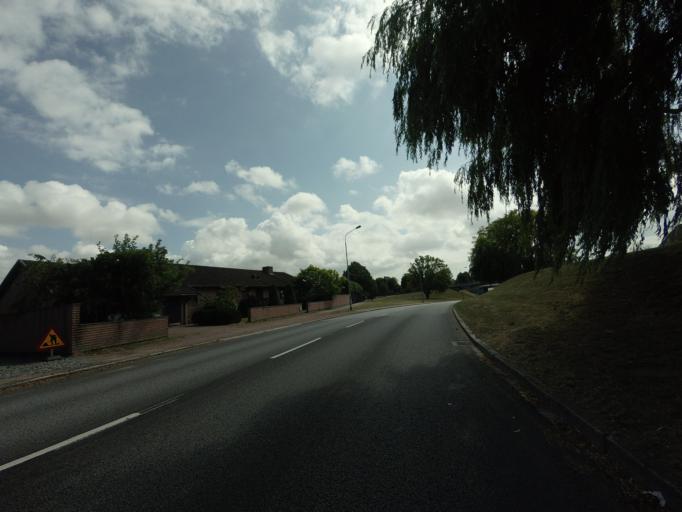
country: SE
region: Skane
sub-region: Malmo
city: Malmoe
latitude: 55.5675
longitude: 12.9964
